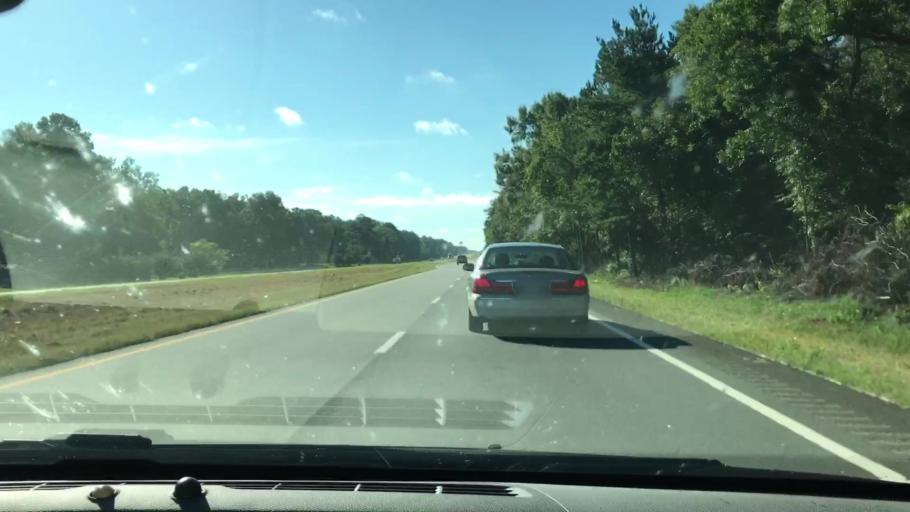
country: US
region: Georgia
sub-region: Lee County
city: Leesburg
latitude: 31.6595
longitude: -84.2749
